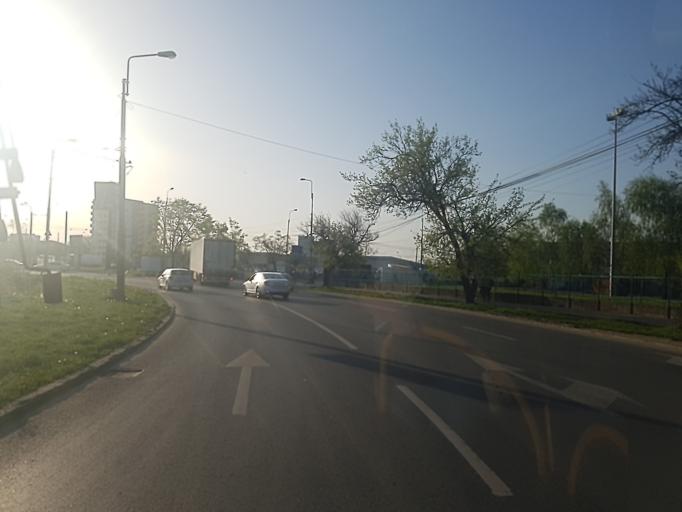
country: RO
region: Timis
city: Timisoara
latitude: 45.7335
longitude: 21.2599
